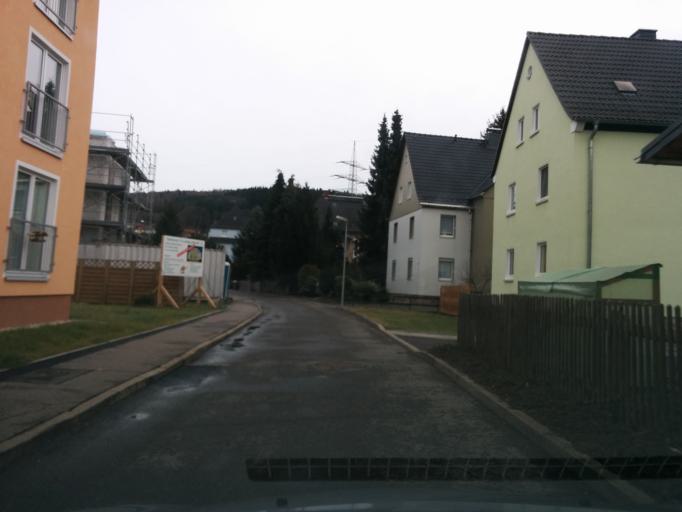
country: DE
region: Saxony
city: Floha
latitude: 50.8408
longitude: 13.0790
